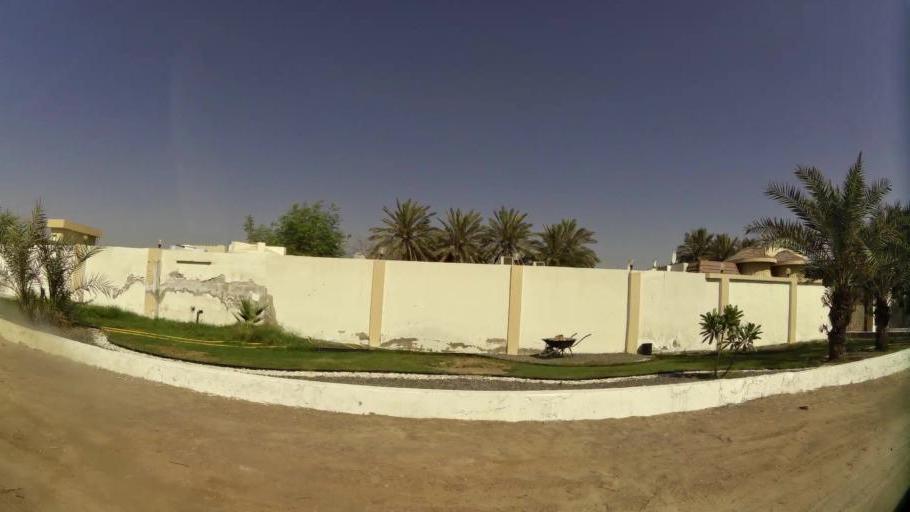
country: AE
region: Ajman
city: Ajman
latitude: 25.4086
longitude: 55.4672
